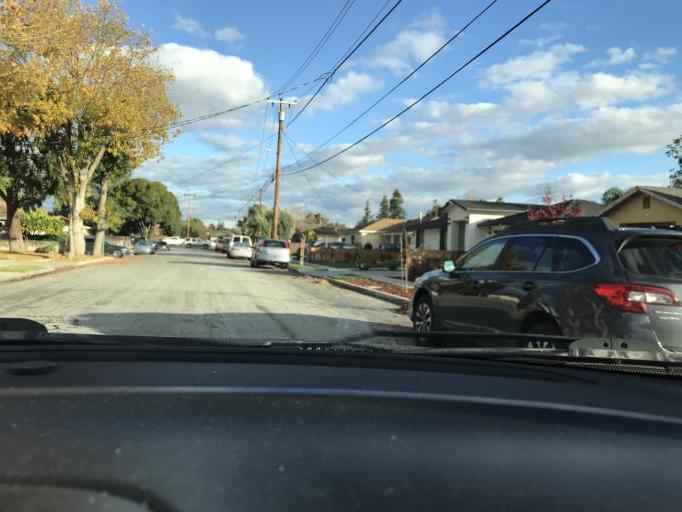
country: US
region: California
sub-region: Santa Clara County
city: Buena Vista
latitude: 37.2933
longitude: -121.9203
